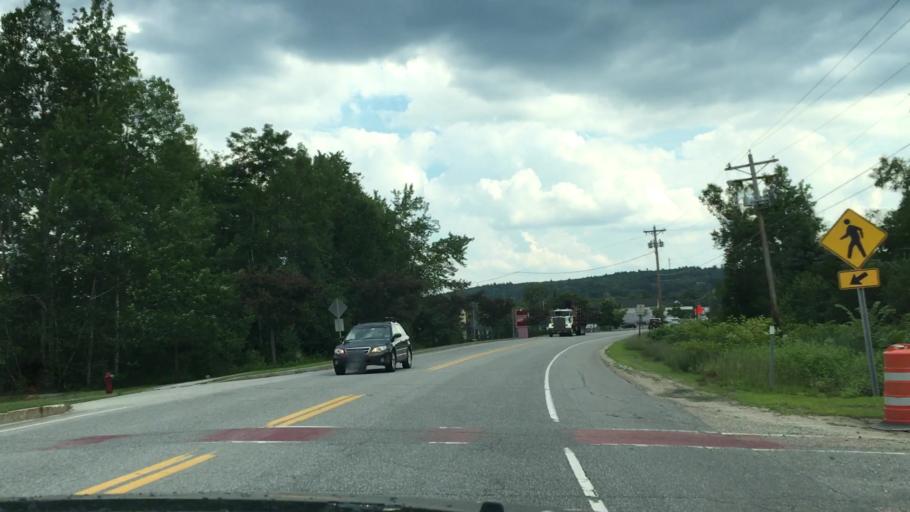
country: US
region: New Hampshire
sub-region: Belknap County
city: Meredith
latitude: 43.6642
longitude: -71.5011
